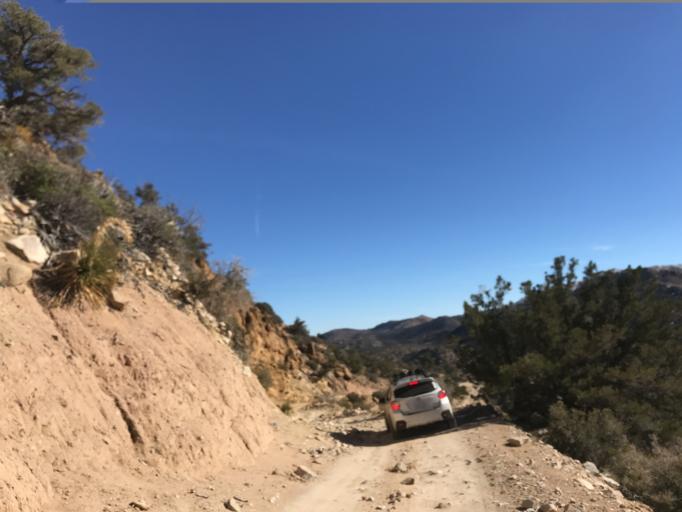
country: US
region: California
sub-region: San Bernardino County
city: Big Bear City
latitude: 34.2304
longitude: -116.6787
